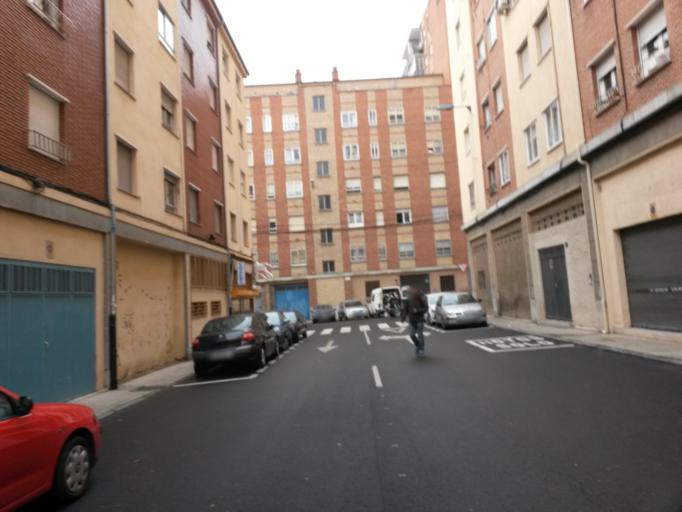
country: ES
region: Castille and Leon
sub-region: Provincia de Salamanca
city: Salamanca
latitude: 40.9782
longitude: -5.6524
